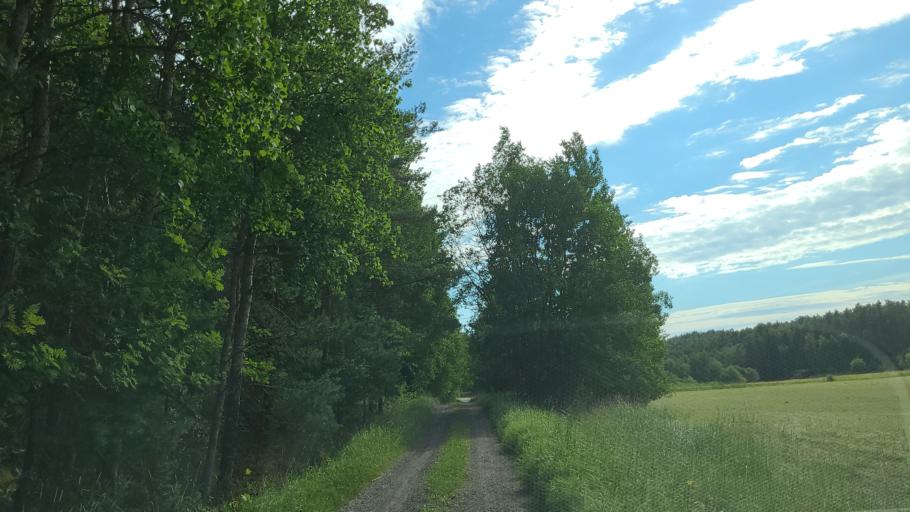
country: FI
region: Varsinais-Suomi
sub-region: Turku
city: Rymaettylae
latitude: 60.2898
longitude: 21.9666
